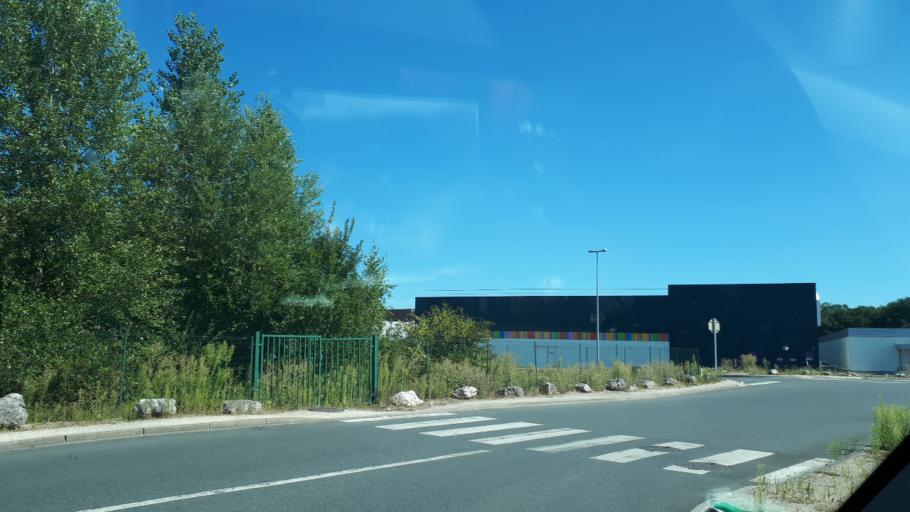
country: FR
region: Centre
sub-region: Departement du Loir-et-Cher
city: Saint-Gervais-la-Foret
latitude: 47.5650
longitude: 1.3734
